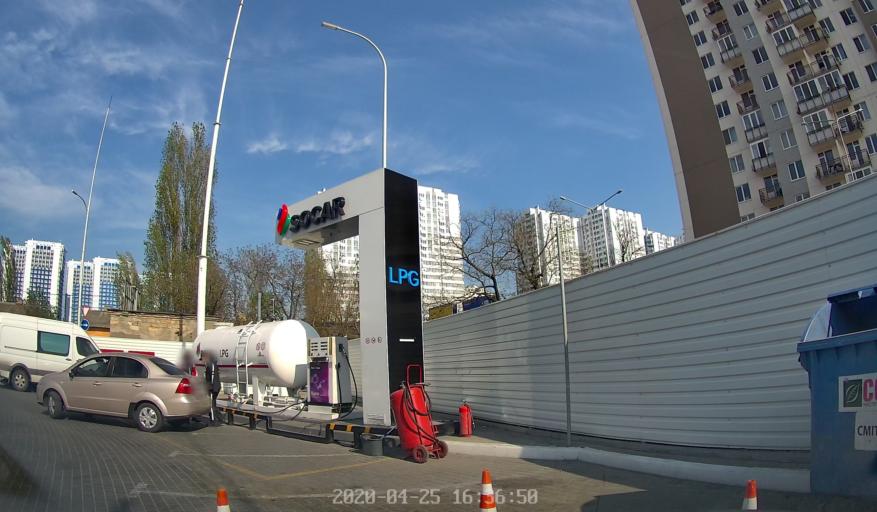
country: NE
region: Zinder
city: Mirriah
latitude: 13.9274
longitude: 9.2170
